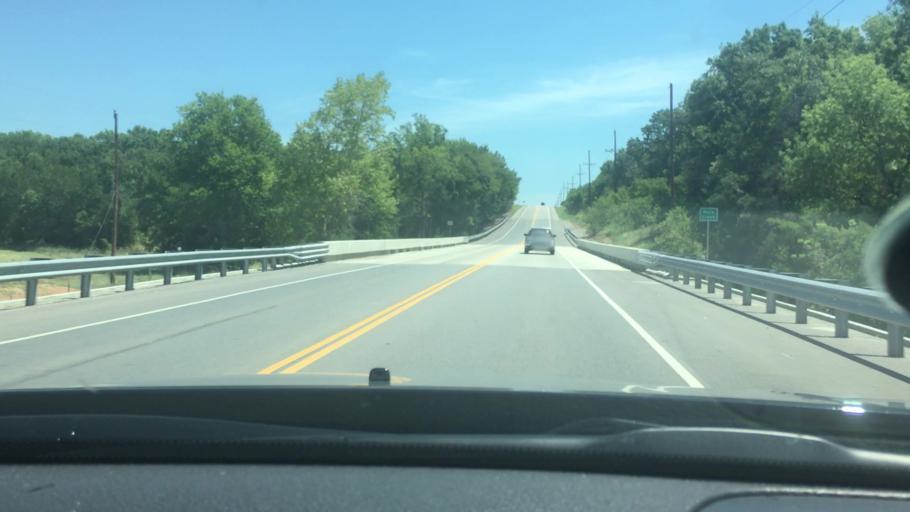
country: US
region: Oklahoma
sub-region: Bryan County
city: Durant
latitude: 34.0072
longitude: -96.1836
